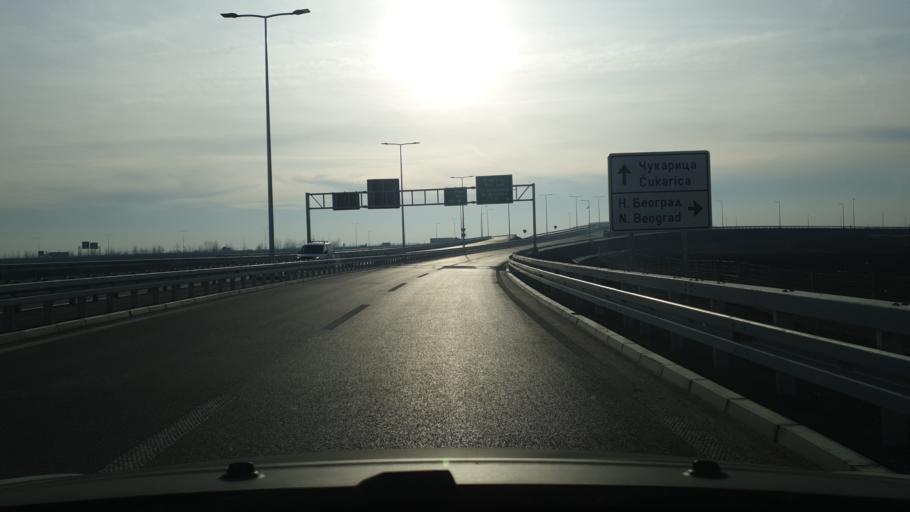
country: RS
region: Central Serbia
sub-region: Belgrade
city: Surcin
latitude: 44.7714
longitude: 20.2795
